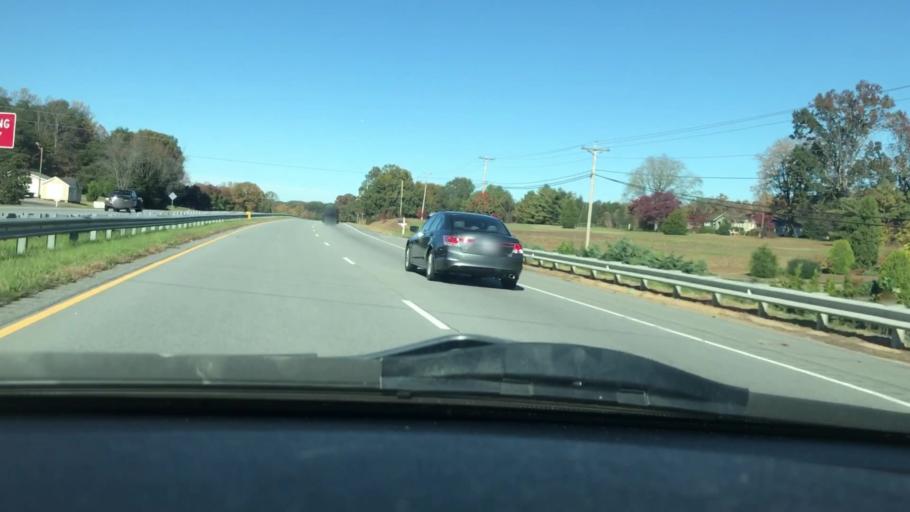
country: US
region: North Carolina
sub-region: Rockingham County
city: Madison
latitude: 36.3316
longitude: -79.9463
